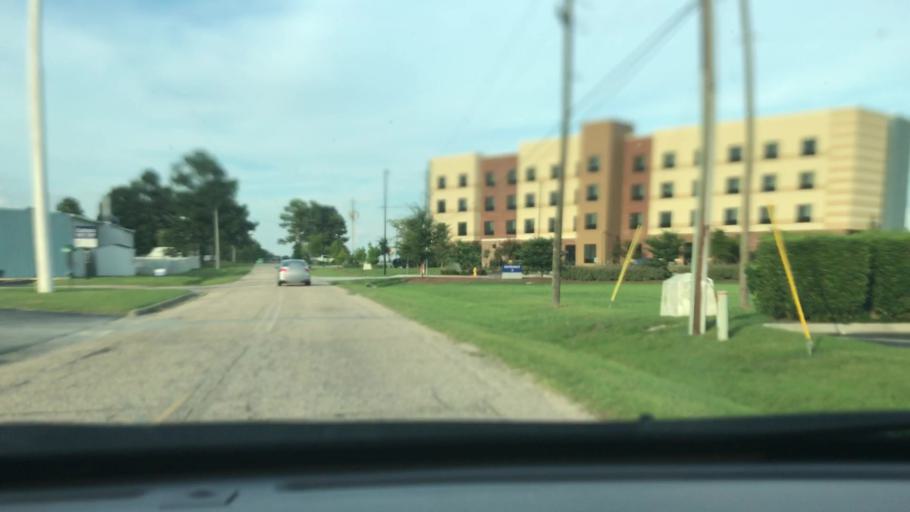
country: US
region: North Carolina
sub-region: Harnett County
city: Dunn
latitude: 35.2946
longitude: -78.6050
